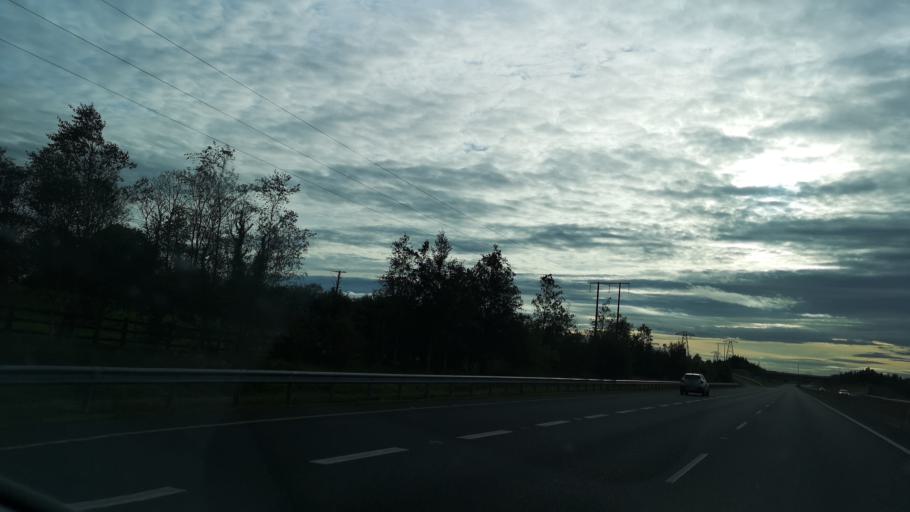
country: IE
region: Connaught
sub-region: County Galway
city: Loughrea
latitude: 53.2653
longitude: -8.6000
